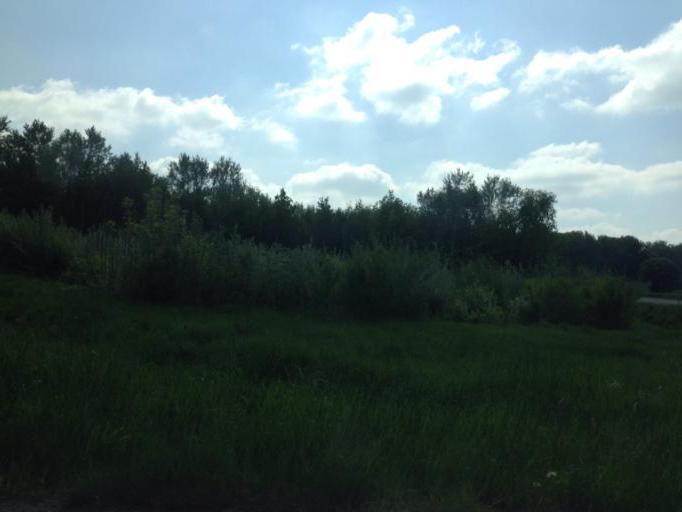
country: DE
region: North Rhine-Westphalia
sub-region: Regierungsbezirk Koln
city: Mechernich
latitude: 50.5757
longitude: 6.6867
